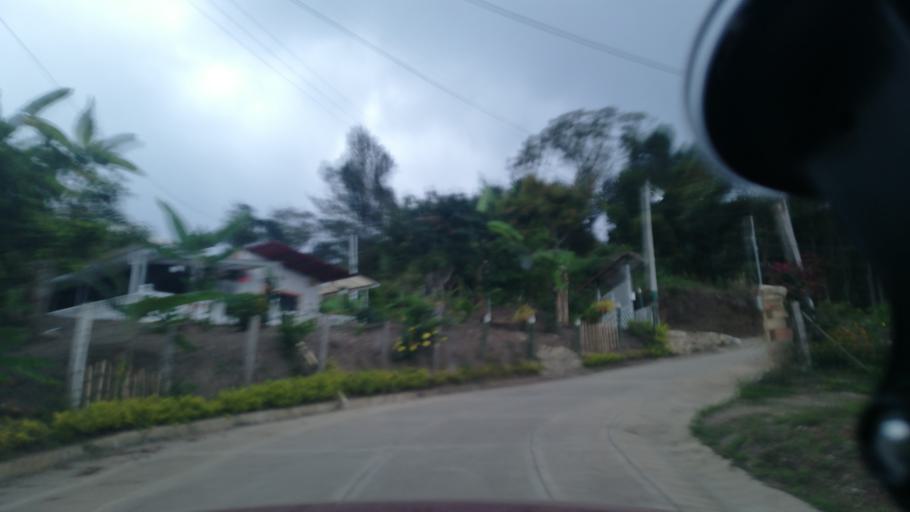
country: CO
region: Cundinamarca
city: San Antonio del Tequendama
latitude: 4.6612
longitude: -74.3983
